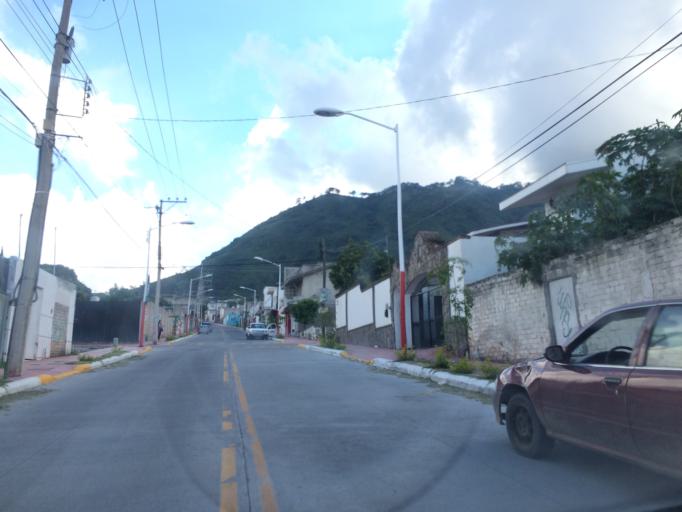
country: MX
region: Nayarit
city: Tepic
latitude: 21.4985
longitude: -104.9159
